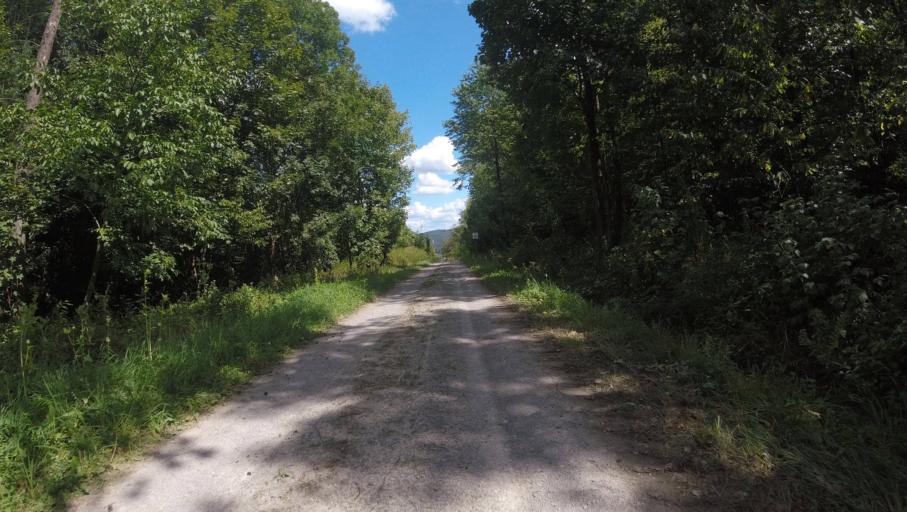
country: DE
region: Baden-Wuerttemberg
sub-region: Regierungsbezirk Stuttgart
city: Oppenweiler
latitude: 48.9887
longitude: 9.4388
